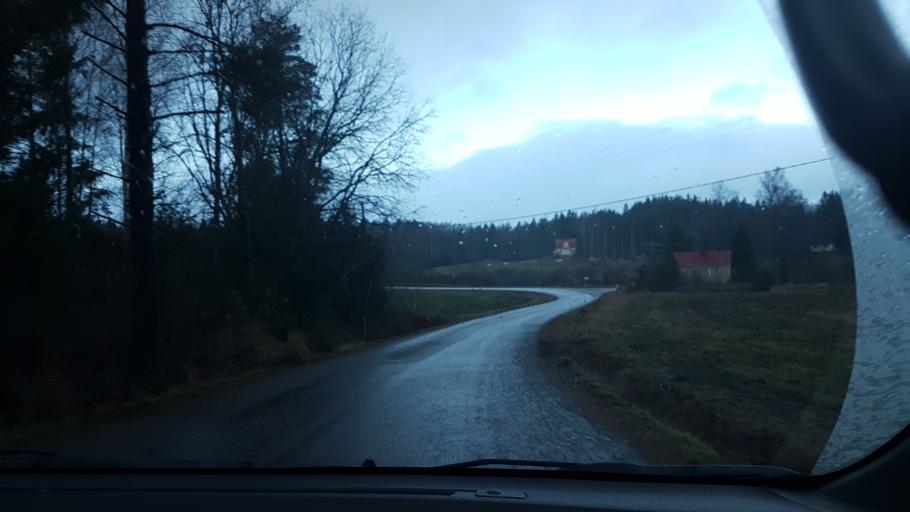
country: FI
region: Uusimaa
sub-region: Helsinki
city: Lohja
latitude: 60.2129
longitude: 24.0998
